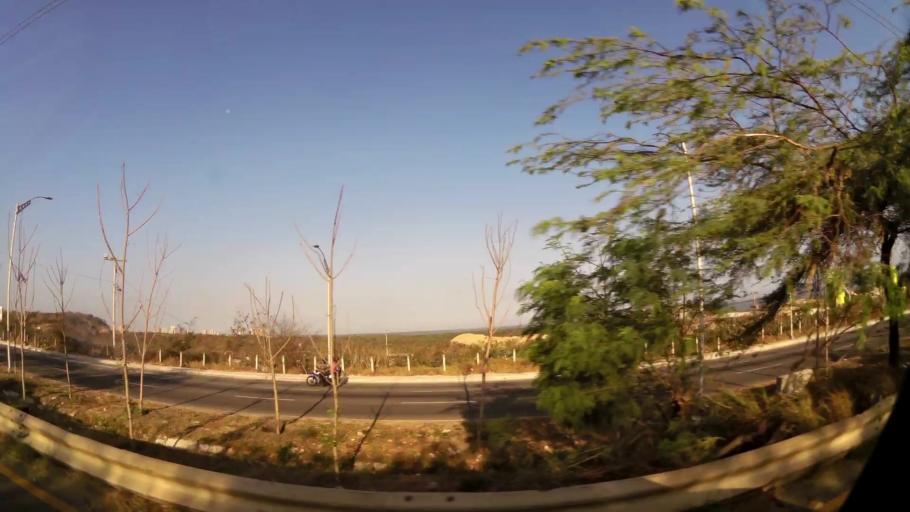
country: CO
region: Atlantico
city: Barranquilla
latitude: 11.0298
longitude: -74.8327
